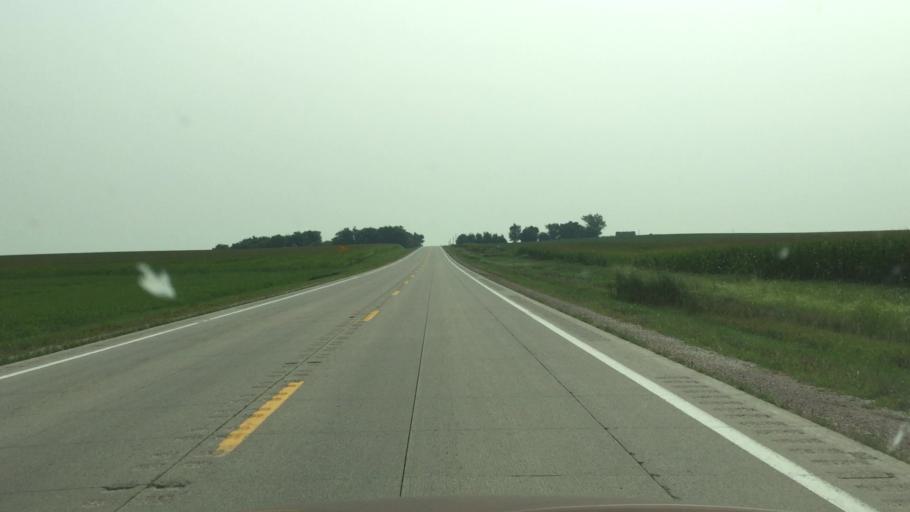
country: US
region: Iowa
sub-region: Osceola County
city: Sibley
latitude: 43.4327
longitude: -95.6704
